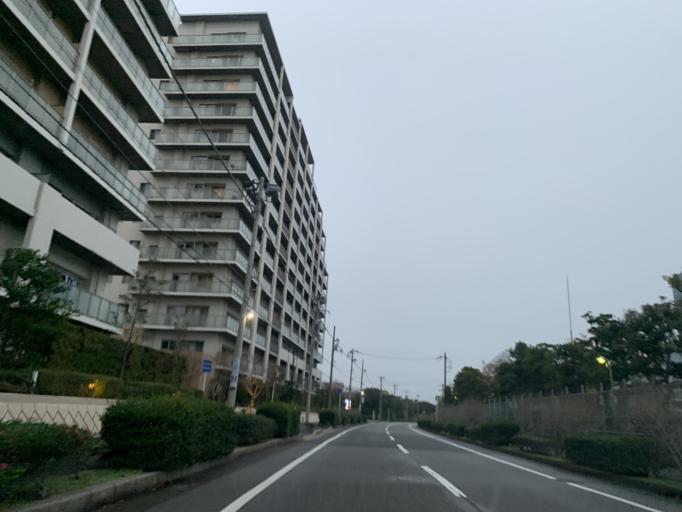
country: JP
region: Chiba
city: Funabashi
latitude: 35.6590
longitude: 140.0372
